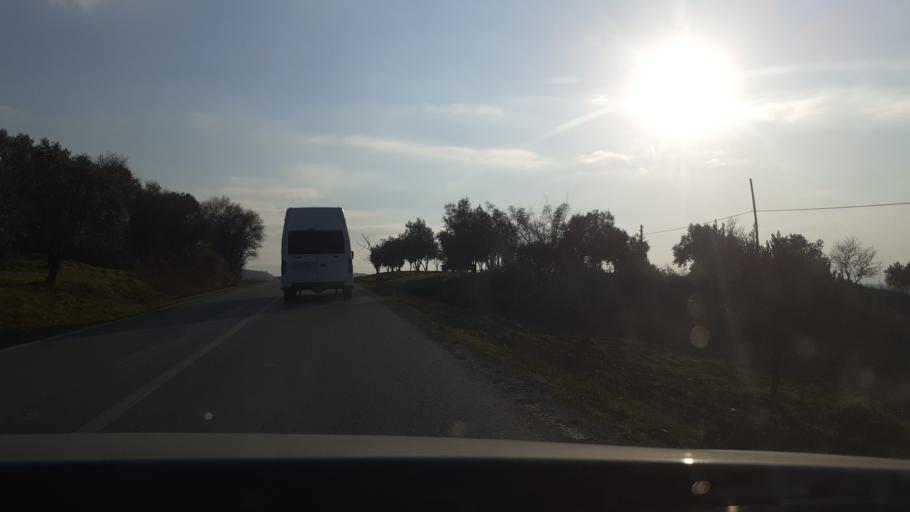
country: TR
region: Hatay
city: Oymakli
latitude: 36.1211
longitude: 36.3057
